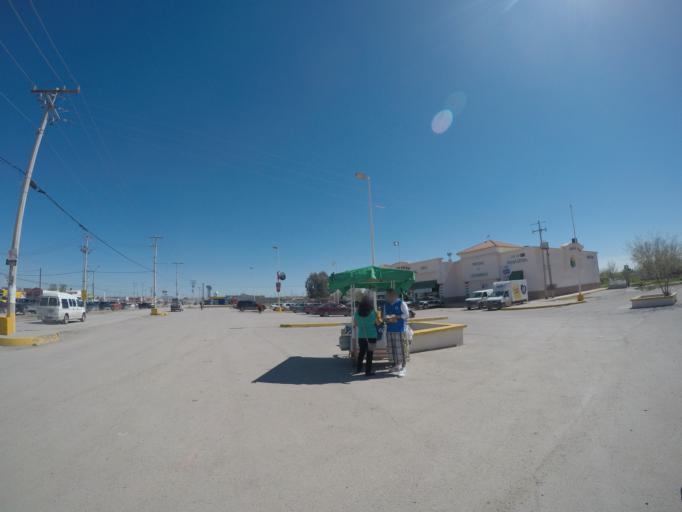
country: US
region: Texas
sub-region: El Paso County
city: Socorro Mission Number 1 Colonia
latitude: 31.6245
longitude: -106.3270
